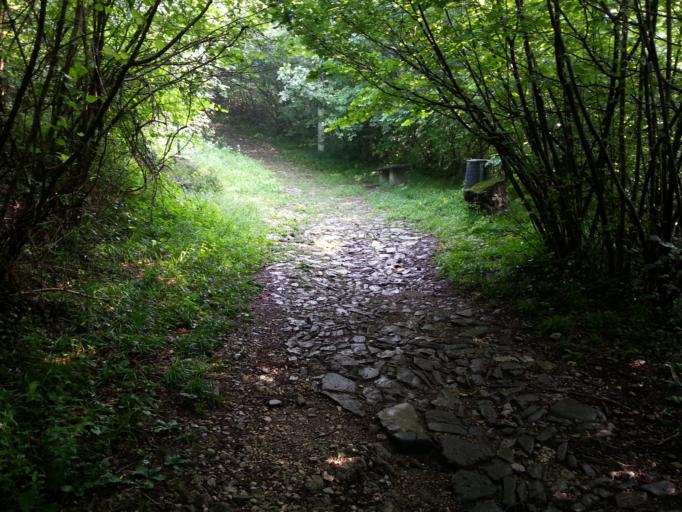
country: IT
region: Lombardy
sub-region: Provincia di Varese
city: Viggiu
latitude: 45.8786
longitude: 8.9020
